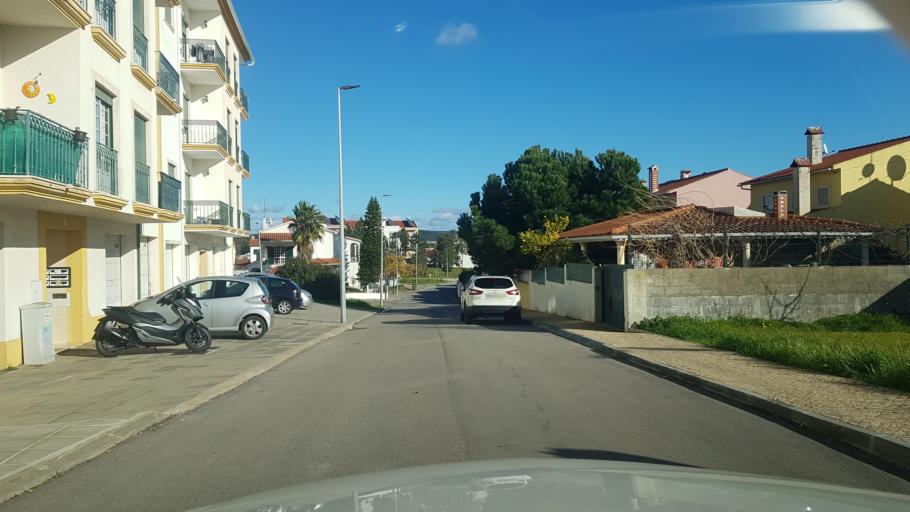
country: PT
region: Santarem
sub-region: Entroncamento
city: Entroncamento
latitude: 39.4744
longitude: -8.4779
